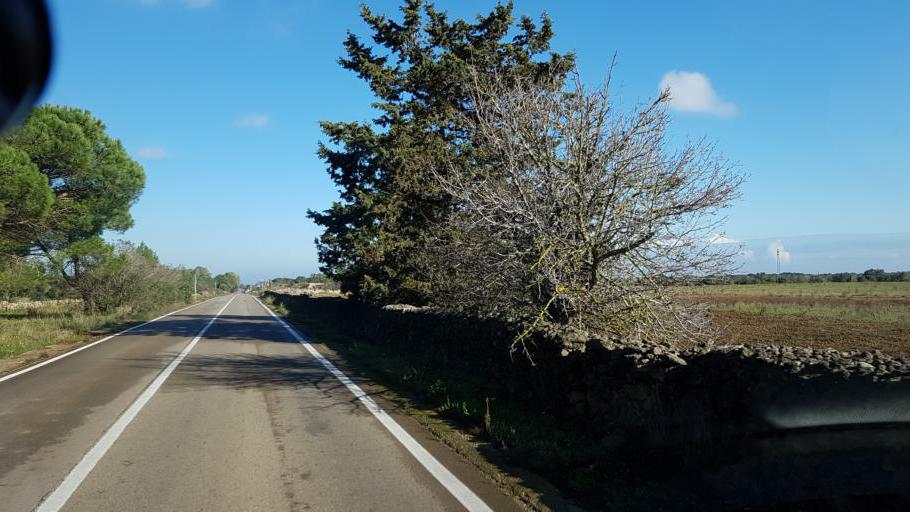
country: IT
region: Apulia
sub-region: Provincia di Lecce
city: Trepuzzi
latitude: 40.4537
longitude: 18.1121
